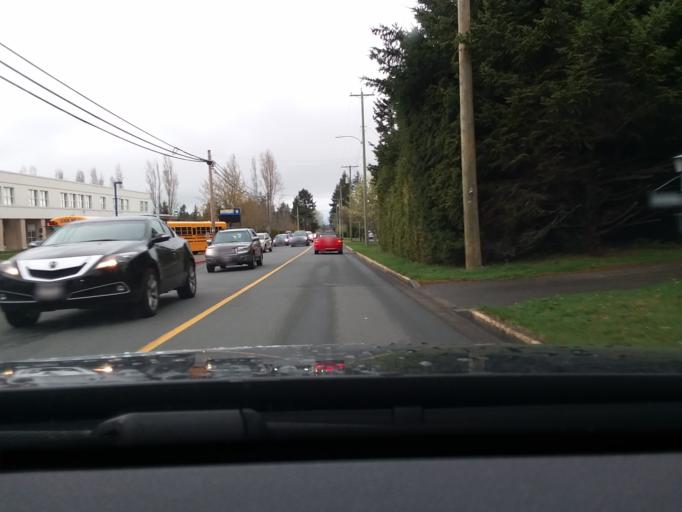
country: CA
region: British Columbia
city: Victoria
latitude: 48.5158
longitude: -123.3741
